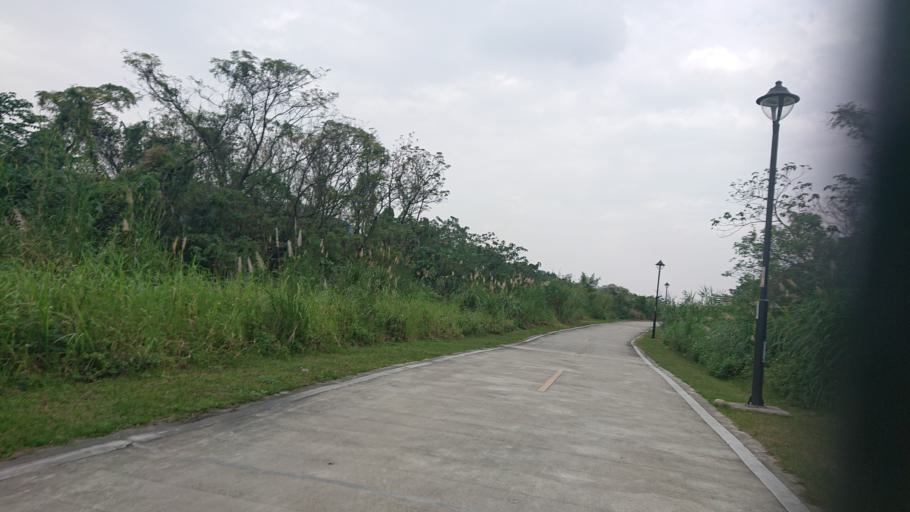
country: TW
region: Taiwan
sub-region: Taoyuan
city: Taoyuan
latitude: 24.9506
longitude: 121.3629
